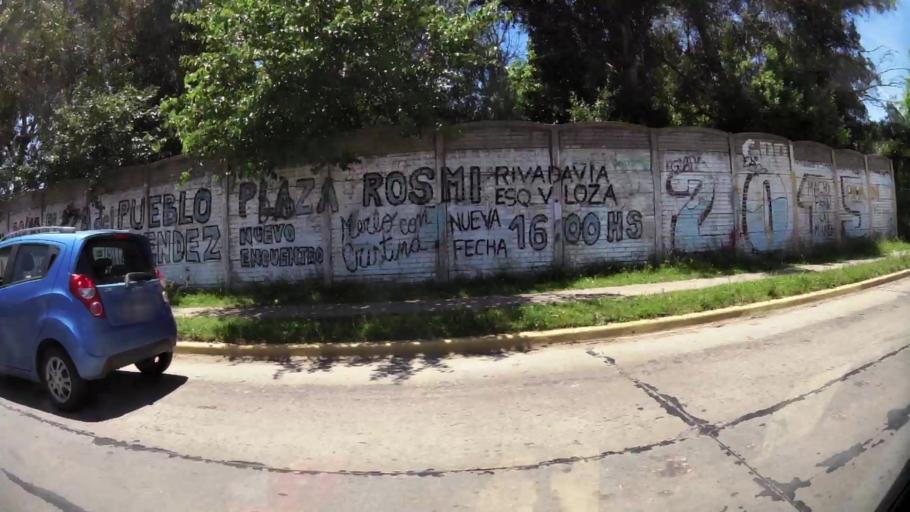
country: AR
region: Buenos Aires
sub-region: Partido de Merlo
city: Merlo
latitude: -34.6583
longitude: -58.7093
